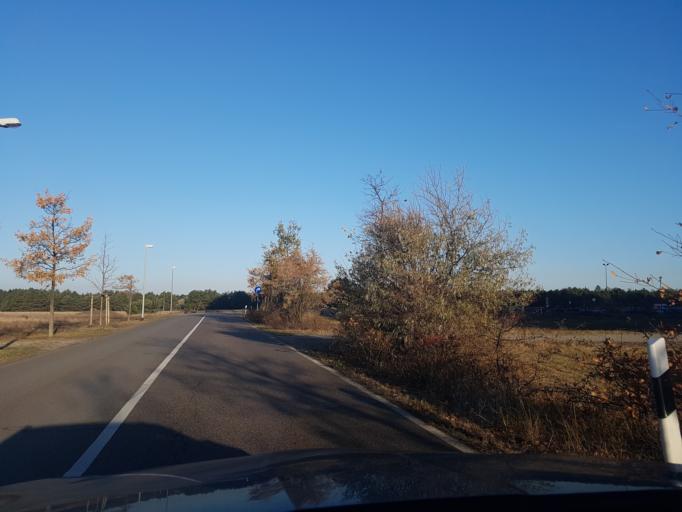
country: DE
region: Brandenburg
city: Halbe
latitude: 52.0389
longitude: 13.7451
